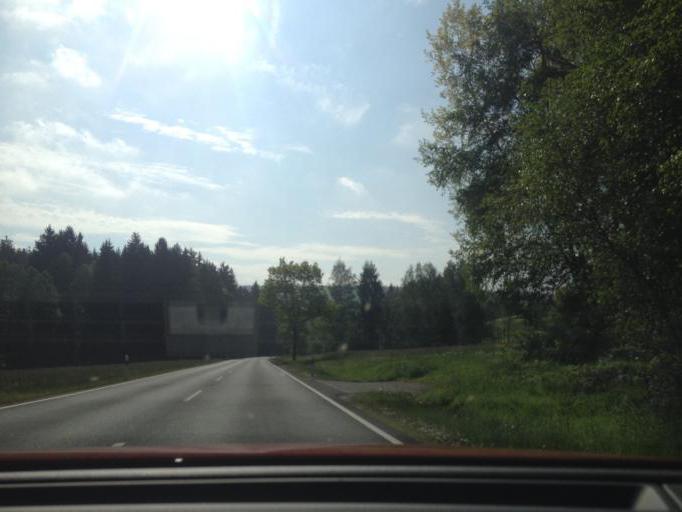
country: DE
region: Bavaria
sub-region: Upper Palatinate
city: Neusorg
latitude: 49.9079
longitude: 11.9610
